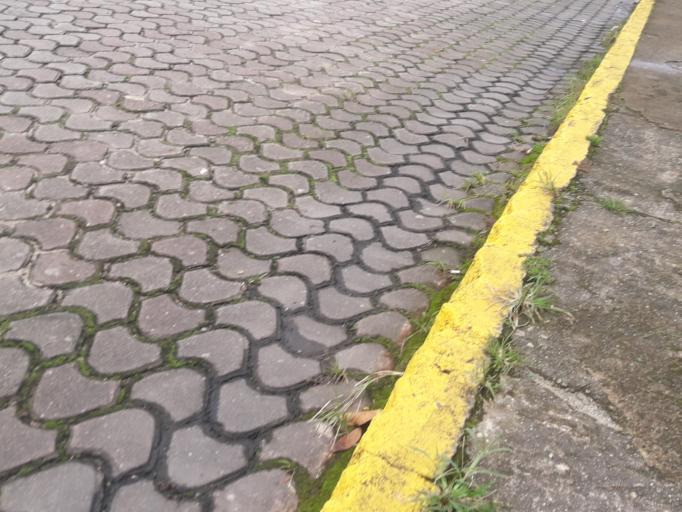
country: EC
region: Napo
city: Tena
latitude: -0.9915
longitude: -77.8128
